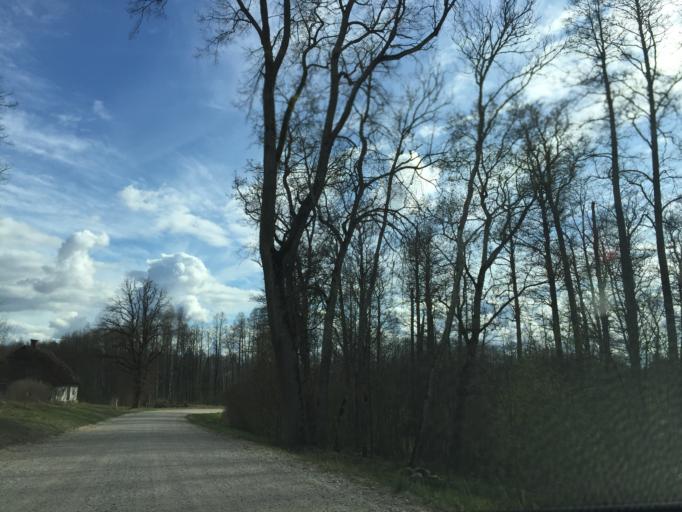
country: LV
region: Burtnieki
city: Matisi
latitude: 57.6130
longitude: 25.0797
